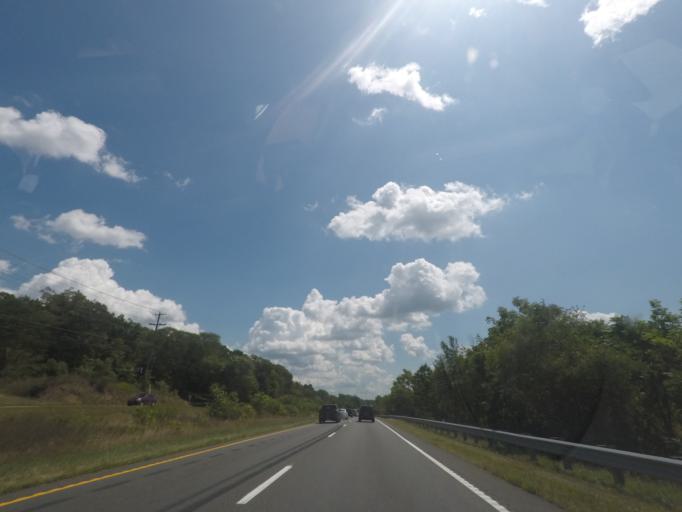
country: US
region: Virginia
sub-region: City of Winchester
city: Winchester
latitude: 39.1557
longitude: -78.1426
